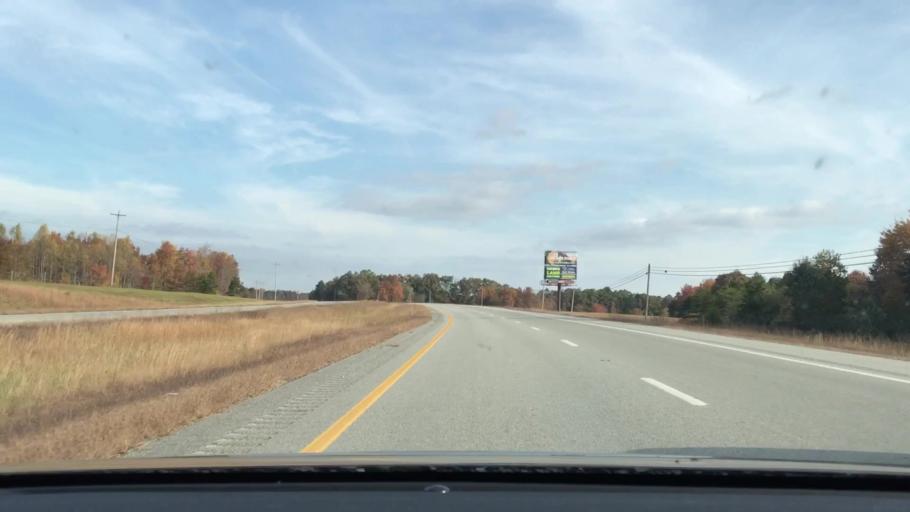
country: US
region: Tennessee
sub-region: Fentress County
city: Grimsley
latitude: 36.3399
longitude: -84.9530
